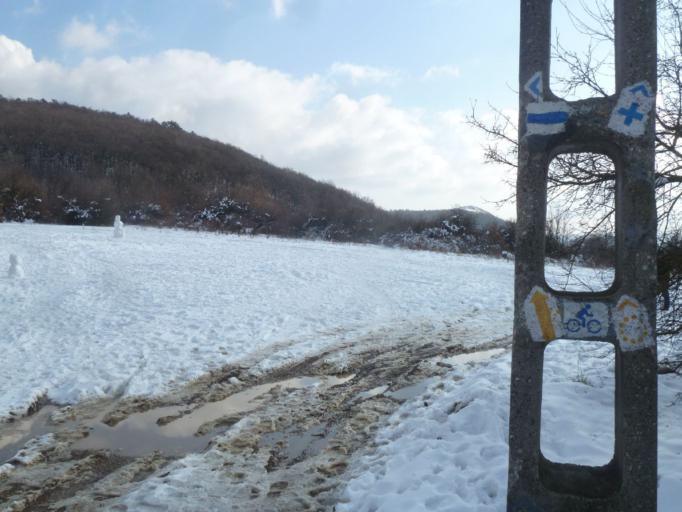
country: HU
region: Pest
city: Urom
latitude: 47.5652
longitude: 18.9892
